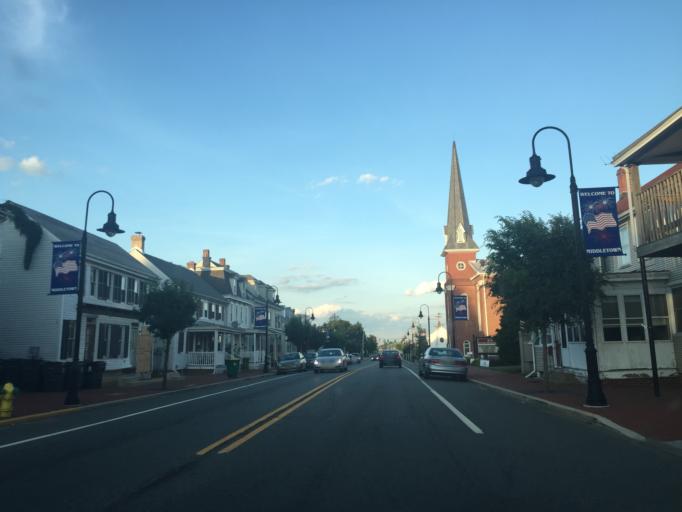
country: US
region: Delaware
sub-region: New Castle County
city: Middletown
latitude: 39.4498
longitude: -75.7149
